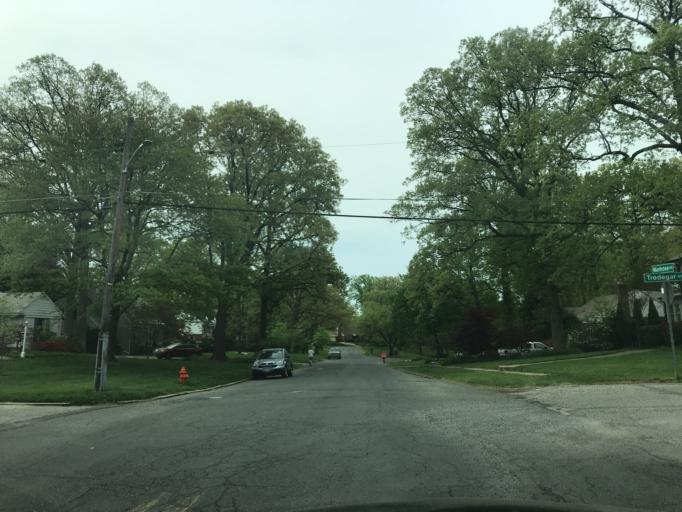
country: US
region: Maryland
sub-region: Baltimore County
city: Catonsville
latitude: 39.2611
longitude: -76.7461
